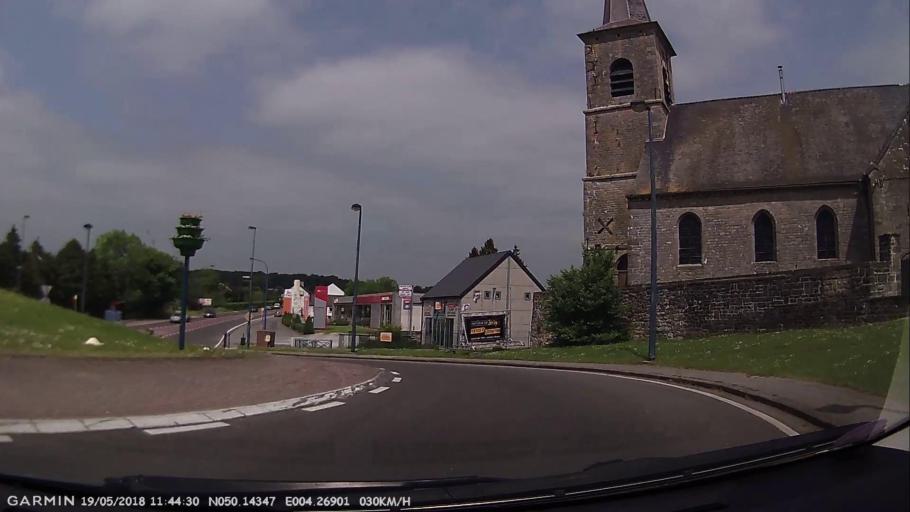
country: BE
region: Wallonia
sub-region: Province du Hainaut
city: Froidchapelle
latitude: 50.1437
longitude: 4.2693
